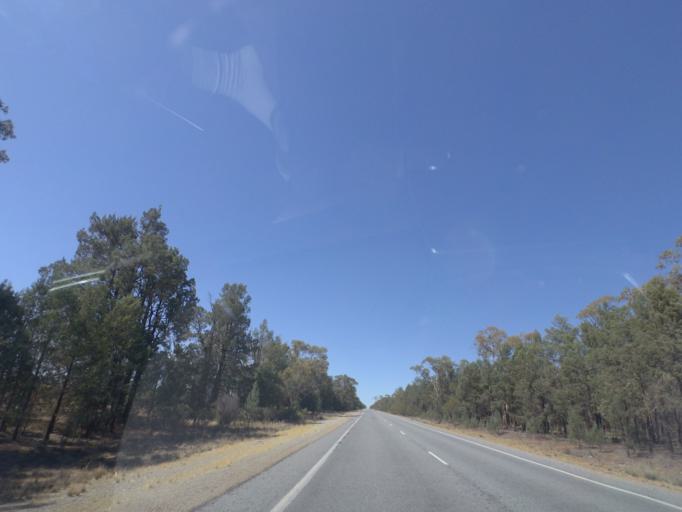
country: AU
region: New South Wales
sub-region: Narrandera
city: Narrandera
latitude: -34.4248
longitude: 146.8443
